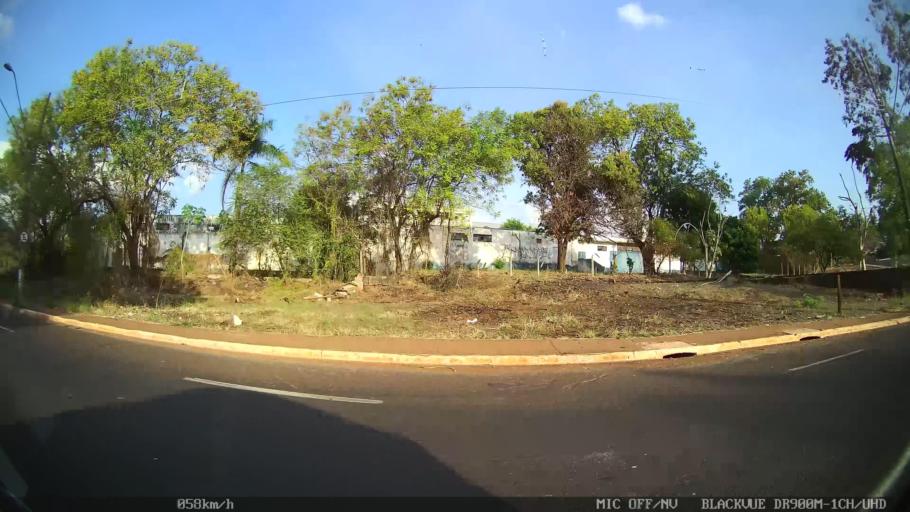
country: BR
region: Sao Paulo
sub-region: Ribeirao Preto
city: Ribeirao Preto
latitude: -21.1599
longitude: -47.8130
